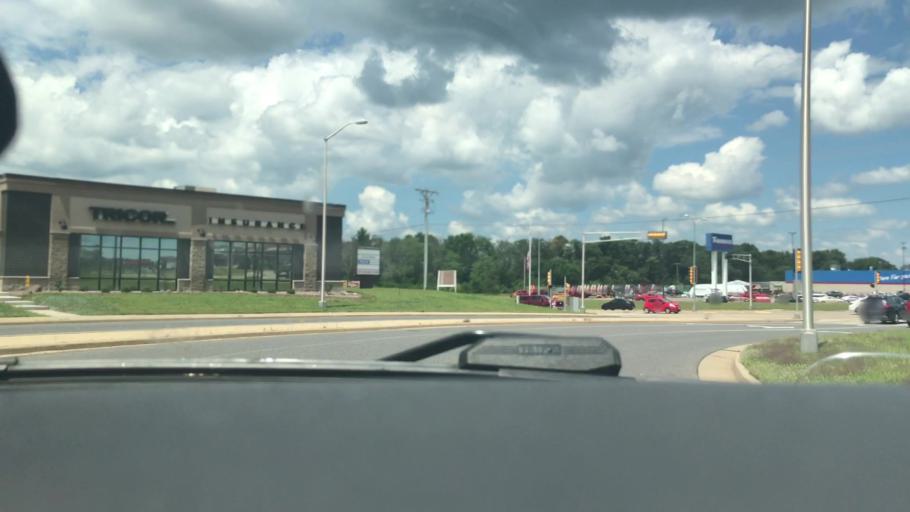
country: US
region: Wisconsin
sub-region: Jackson County
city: Black River Falls
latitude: 44.2937
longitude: -90.8333
